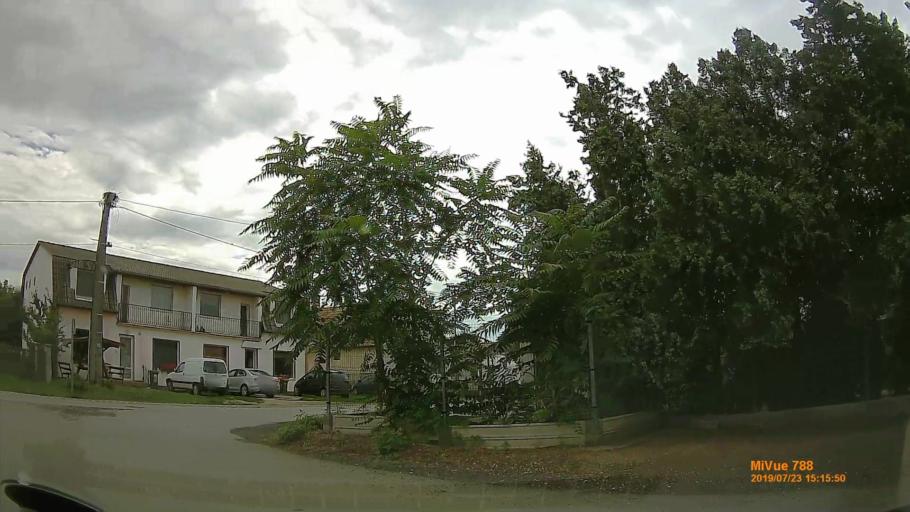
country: HU
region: Szabolcs-Szatmar-Bereg
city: Nyiregyhaza
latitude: 47.9136
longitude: 21.7610
